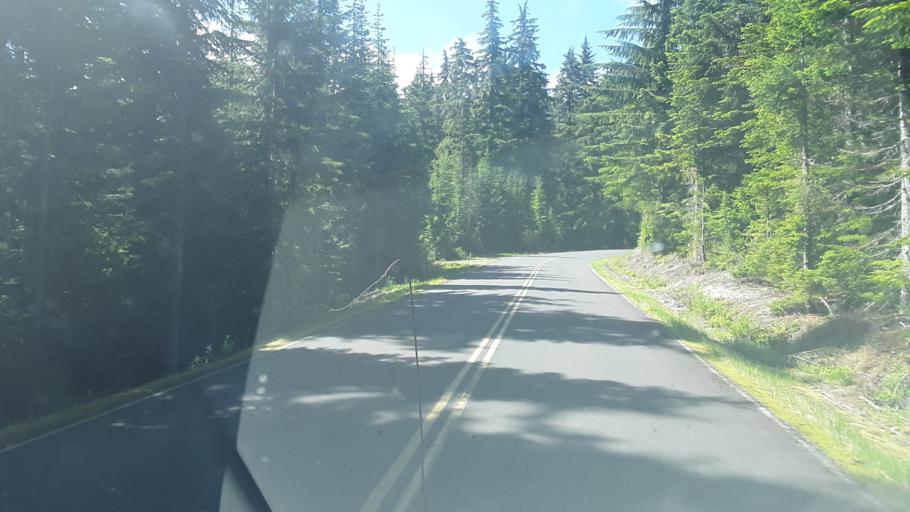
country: US
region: Washington
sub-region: Lewis County
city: Morton
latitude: 46.2932
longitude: -121.9723
